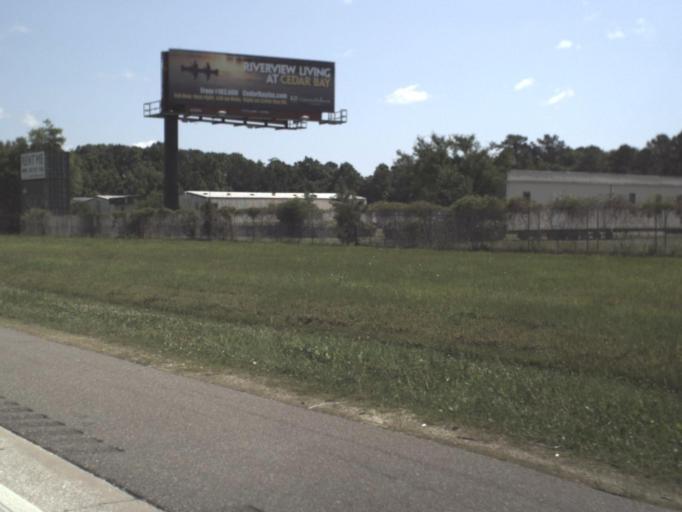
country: US
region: Florida
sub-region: Duval County
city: Jacksonville
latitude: 30.4146
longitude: -81.6569
